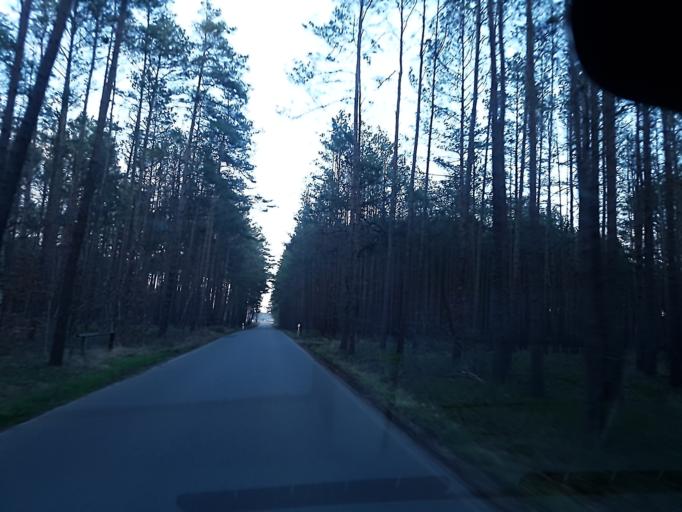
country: DE
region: Brandenburg
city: Ruckersdorf
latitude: 51.5902
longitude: 13.5946
